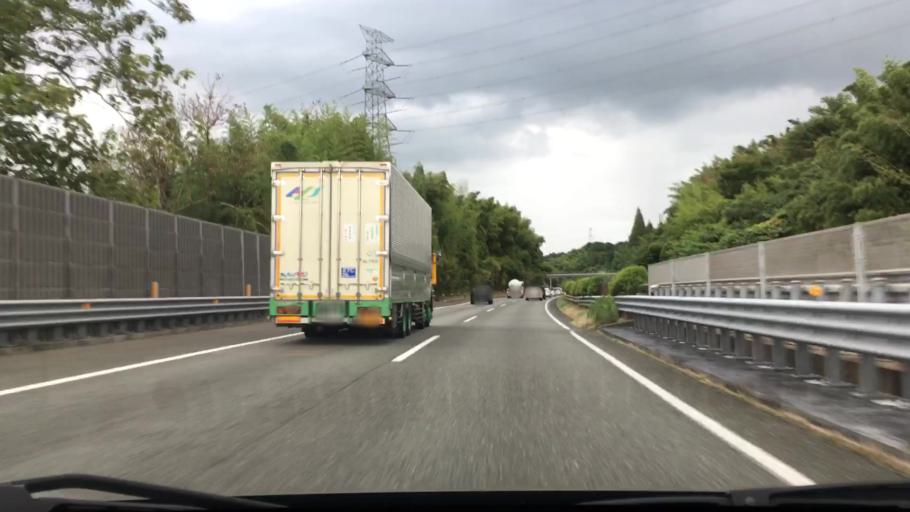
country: JP
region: Fukuoka
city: Miyata
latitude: 33.7487
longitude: 130.5916
